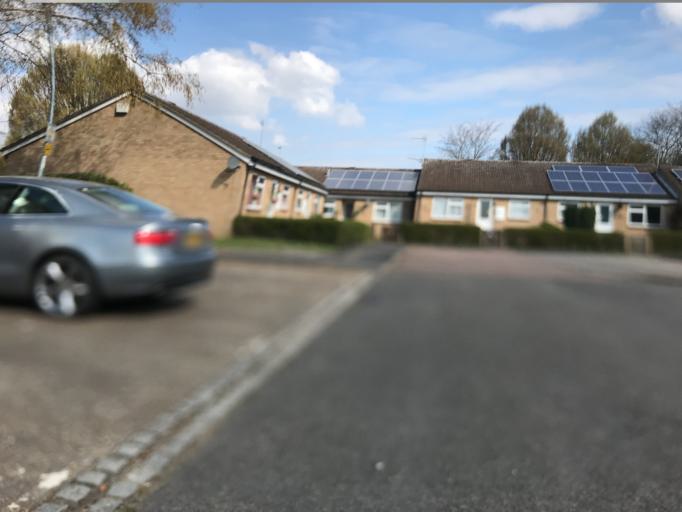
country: GB
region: England
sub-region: Cambridgeshire
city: Sawston
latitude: 52.1512
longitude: 0.1399
